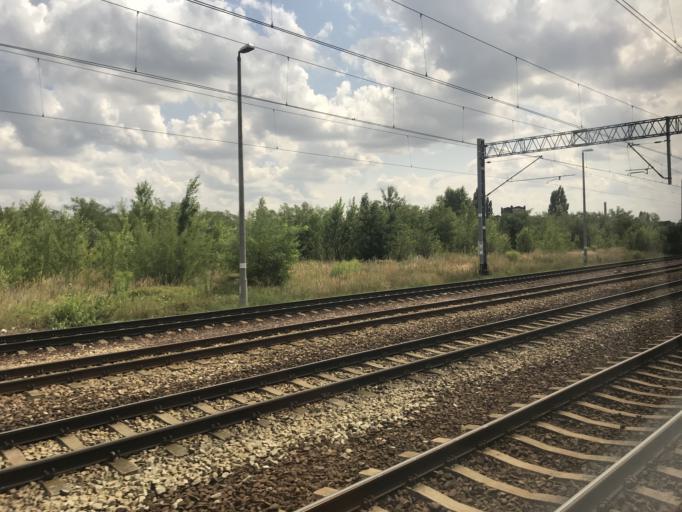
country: PL
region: Greater Poland Voivodeship
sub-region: Poznan
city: Poznan
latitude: 52.3901
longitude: 16.9068
